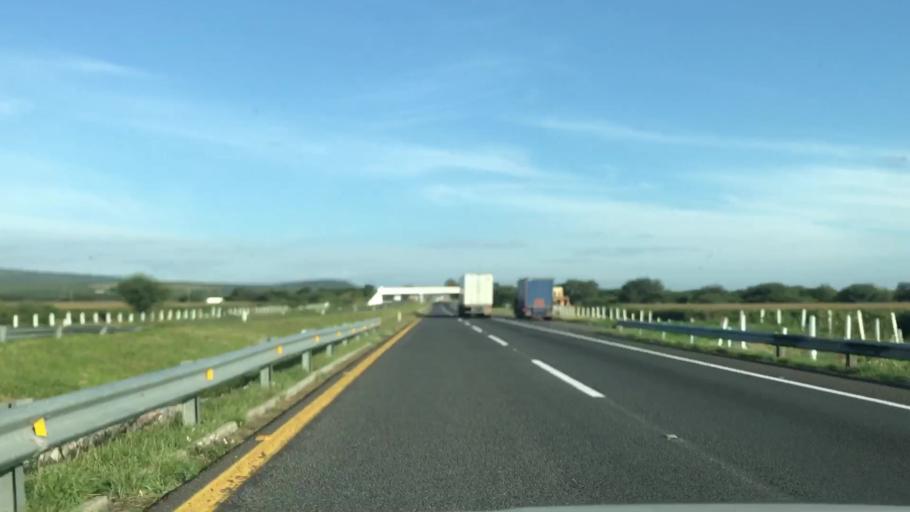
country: MX
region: Jalisco
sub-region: Lagos de Moreno
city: Cristeros [Fraccionamiento]
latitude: 21.2373
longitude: -101.9352
